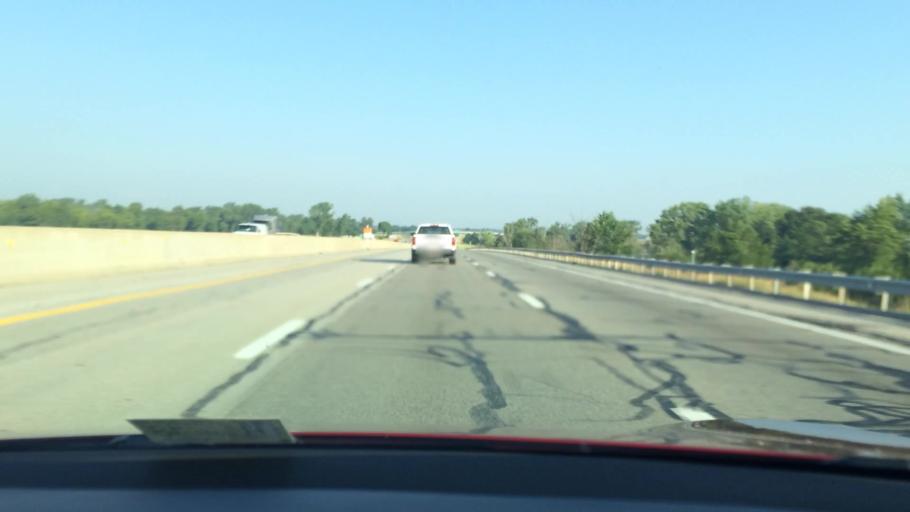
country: US
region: Ohio
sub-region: Ottawa County
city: Elmore
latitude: 41.4495
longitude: -83.2628
